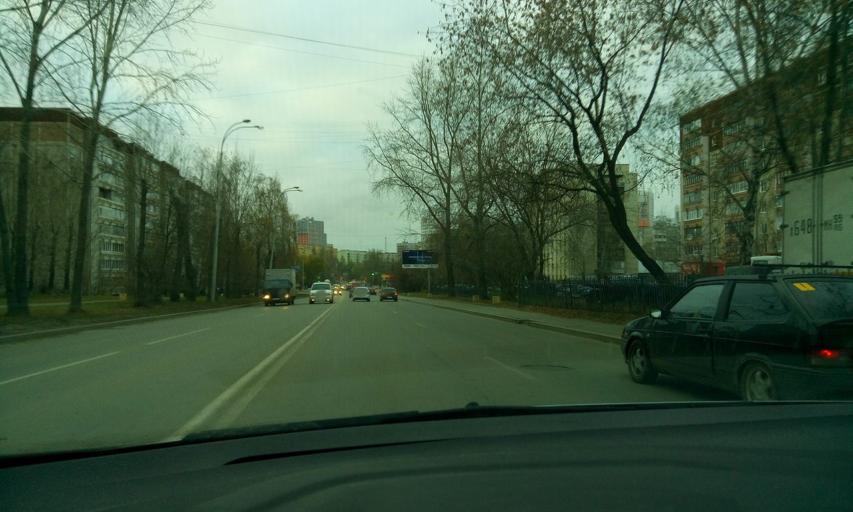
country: RU
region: Sverdlovsk
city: Yekaterinburg
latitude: 56.9007
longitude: 60.6268
